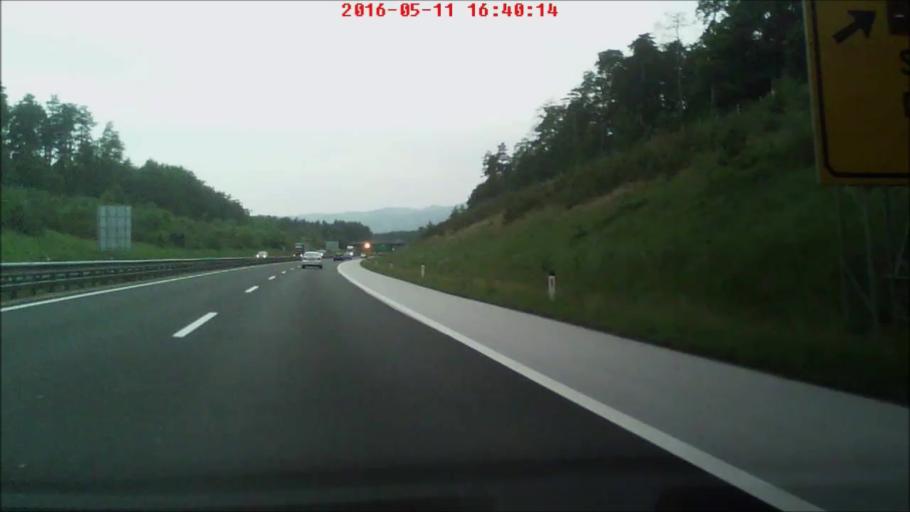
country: SI
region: Miklavz na Dravskem Polju
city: Miklavz na Dravskem Polju
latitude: 46.5235
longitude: 15.6920
